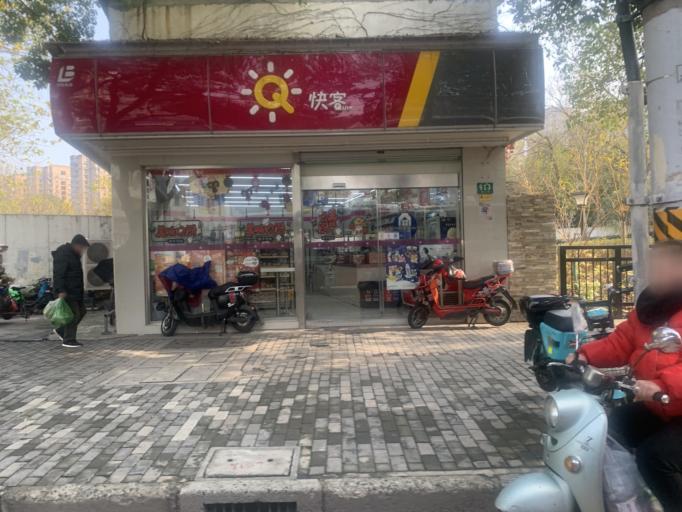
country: CN
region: Shanghai Shi
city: Huamu
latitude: 31.1825
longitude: 121.5157
